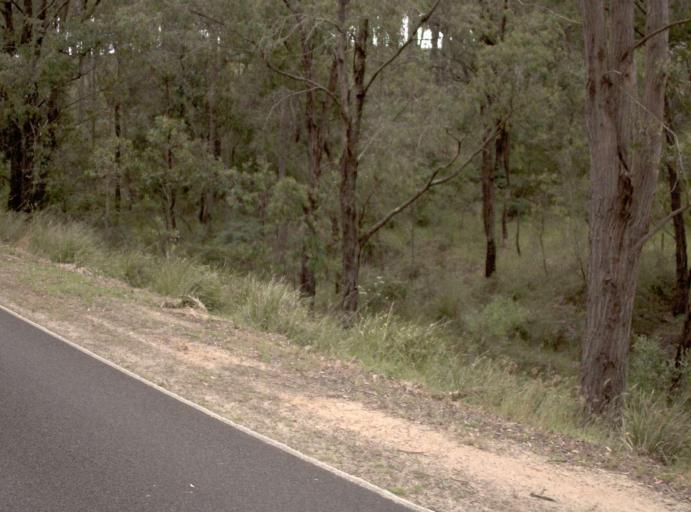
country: AU
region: Victoria
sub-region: Latrobe
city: Traralgon
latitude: -38.4115
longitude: 146.8188
